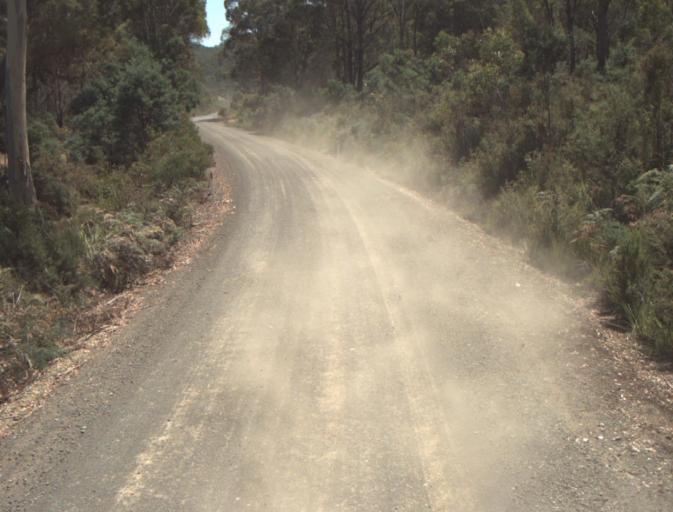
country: AU
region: Tasmania
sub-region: Launceston
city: Mayfield
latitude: -41.2752
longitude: 147.1076
